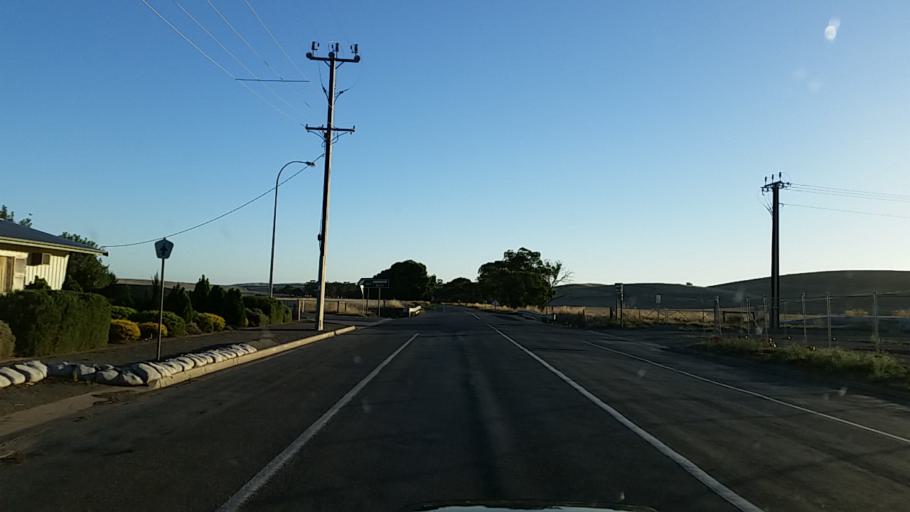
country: AU
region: South Australia
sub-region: Northern Areas
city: Jamestown
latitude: -33.5007
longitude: 138.6068
